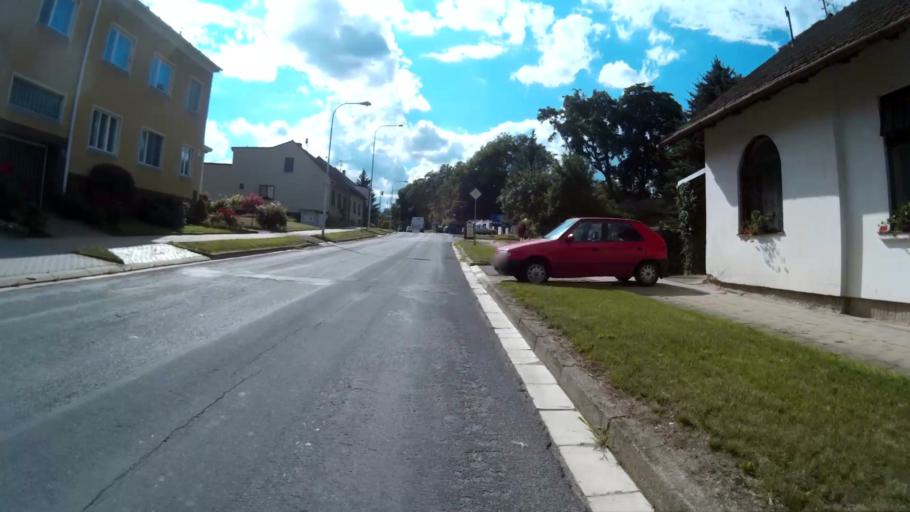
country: CZ
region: South Moravian
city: Strelice
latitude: 49.1532
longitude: 16.4865
